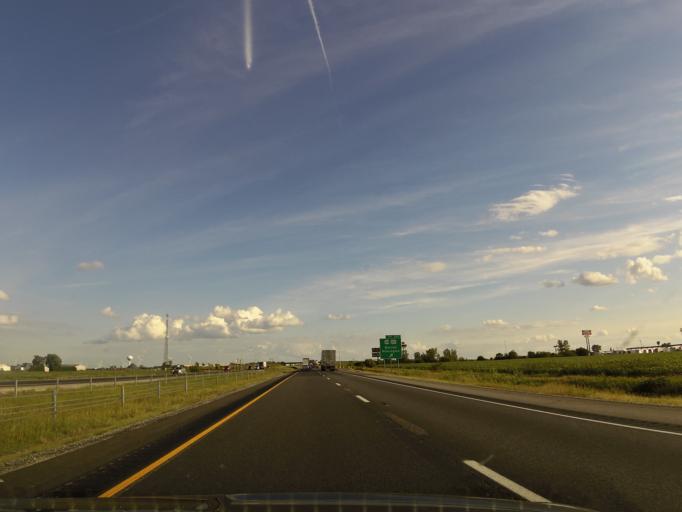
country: US
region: Indiana
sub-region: Jasper County
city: Remington
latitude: 40.7725
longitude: -87.1241
